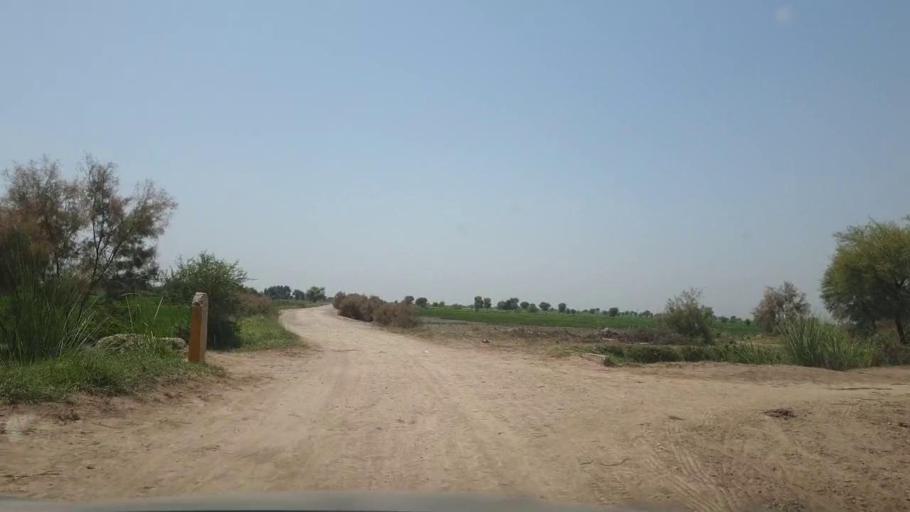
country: PK
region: Sindh
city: Warah
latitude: 27.4891
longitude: 67.7396
